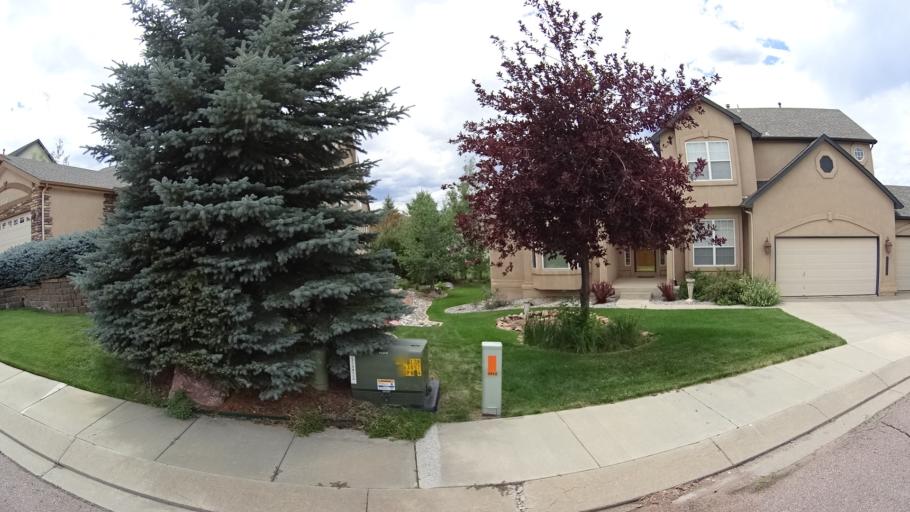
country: US
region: Colorado
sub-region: El Paso County
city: Gleneagle
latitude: 39.0172
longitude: -104.8072
